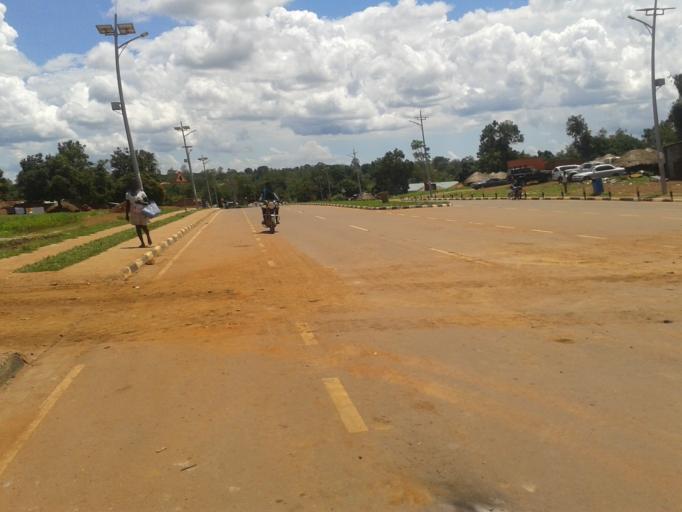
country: UG
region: Northern Region
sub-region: Gulu District
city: Gulu
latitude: 2.7637
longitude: 32.2968
